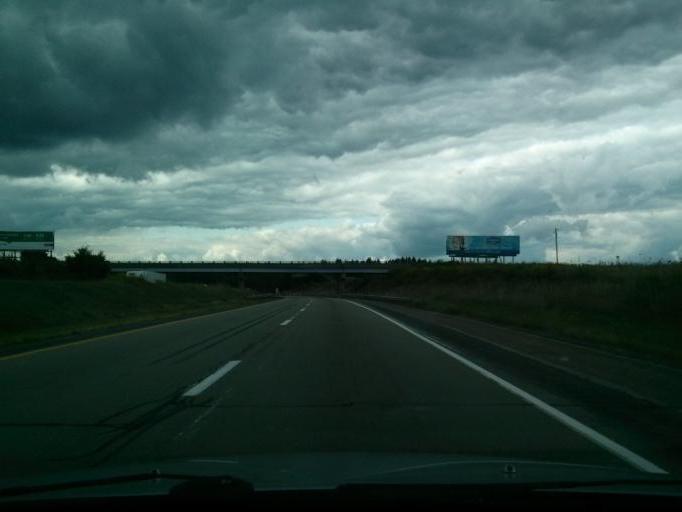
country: US
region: Pennsylvania
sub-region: Clarion County
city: Clarion
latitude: 41.1878
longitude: -79.2348
